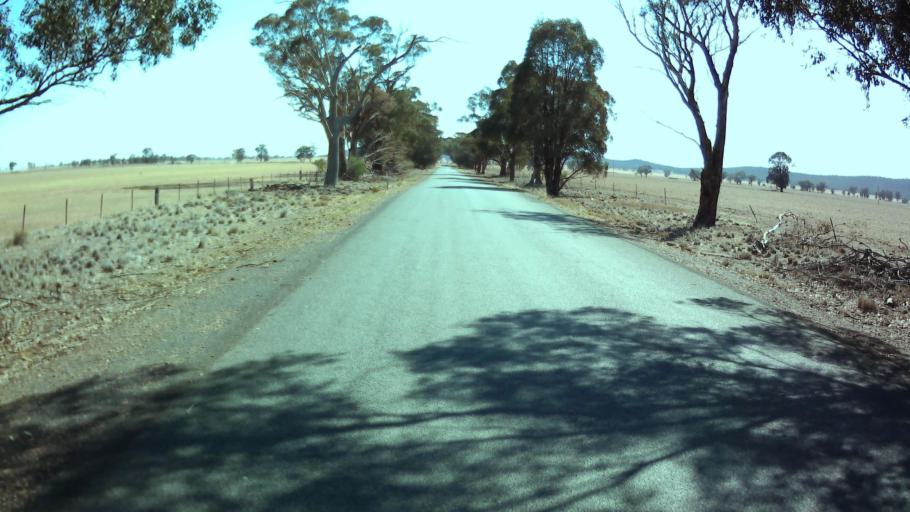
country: AU
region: New South Wales
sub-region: Weddin
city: Grenfell
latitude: -33.7092
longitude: 147.9135
